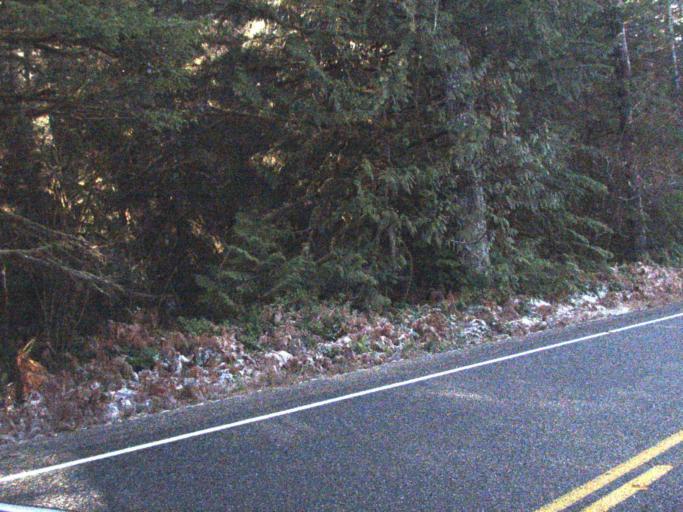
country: US
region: Washington
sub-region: Snohomish County
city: Darrington
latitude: 48.2840
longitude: -121.5750
